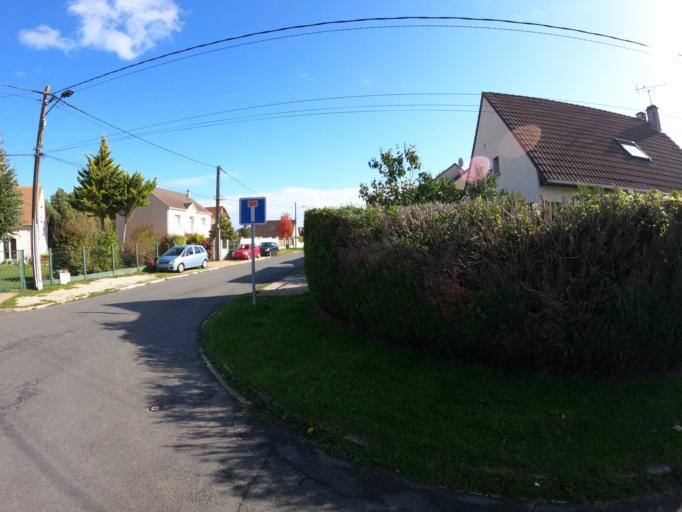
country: FR
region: Ile-de-France
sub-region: Departement de Seine-et-Marne
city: Montry
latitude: 48.8873
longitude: 2.8351
